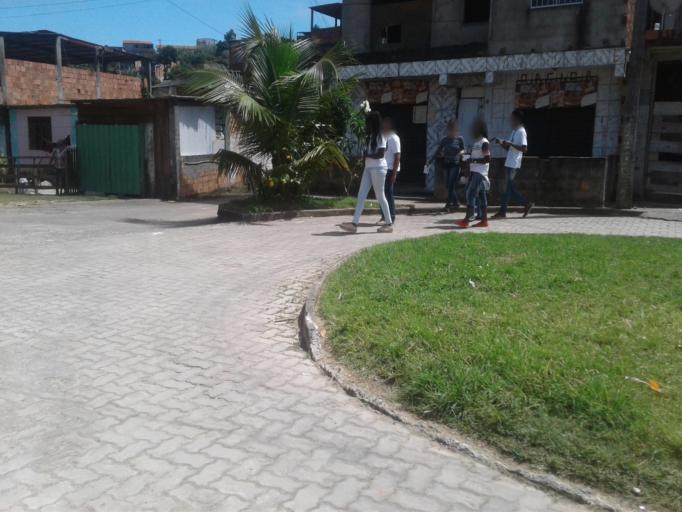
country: BR
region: Bahia
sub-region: Salvador
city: Salvador
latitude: -12.8808
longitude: -38.4726
